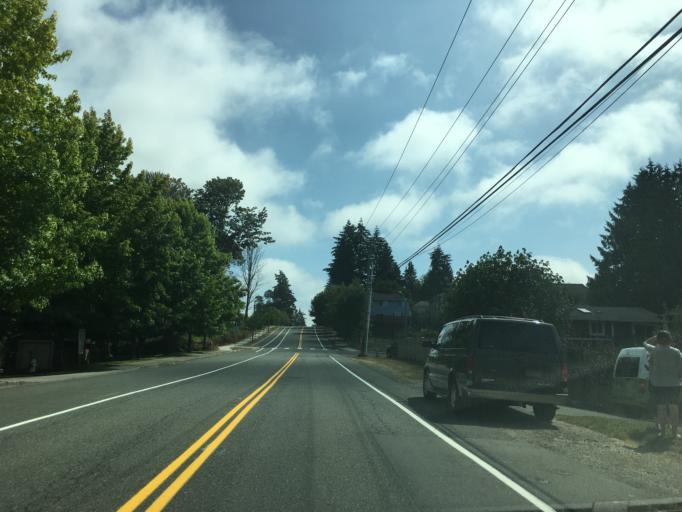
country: US
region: Washington
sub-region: King County
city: Inglewood-Finn Hill
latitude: 47.7189
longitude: -122.2357
